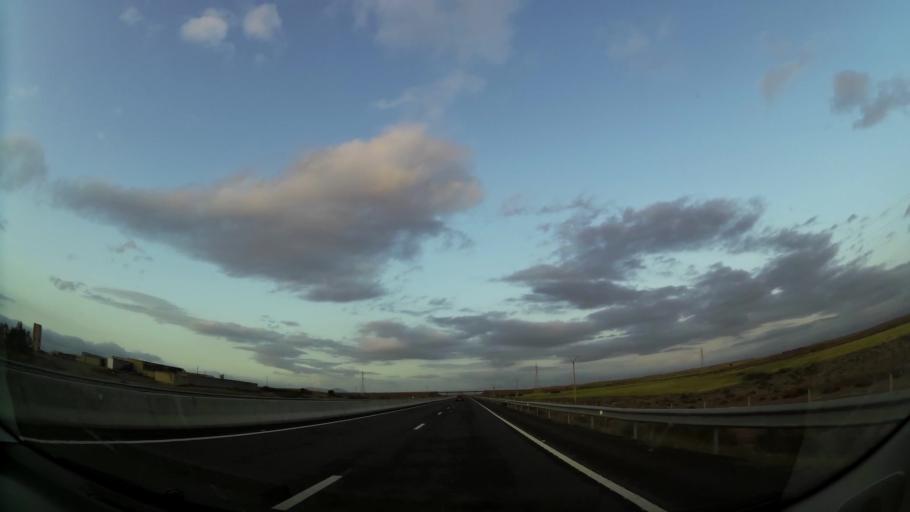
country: MA
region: Oriental
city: Taourirt
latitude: 34.5500
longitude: -2.8667
